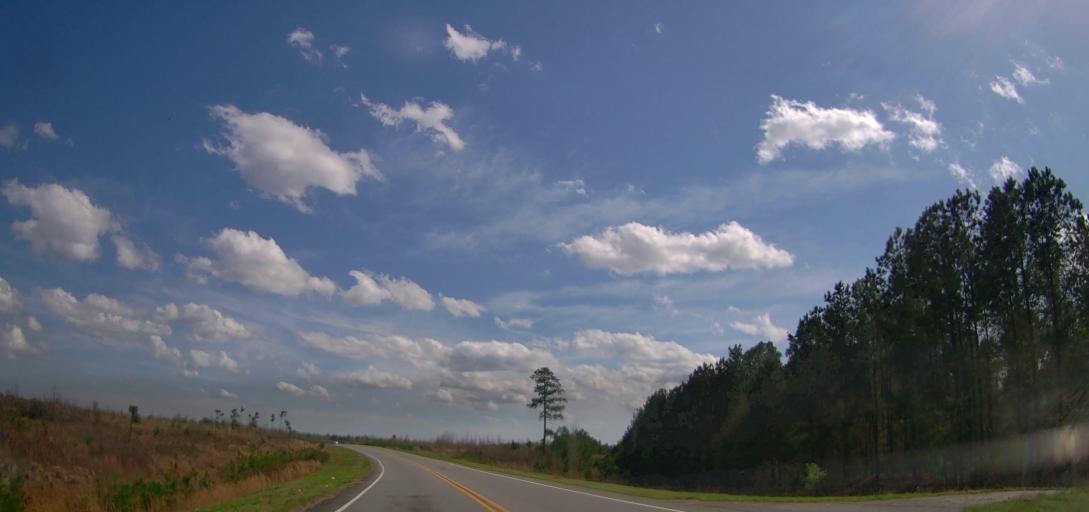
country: US
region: Georgia
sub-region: Wilkinson County
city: Gordon
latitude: 32.9423
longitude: -83.2895
